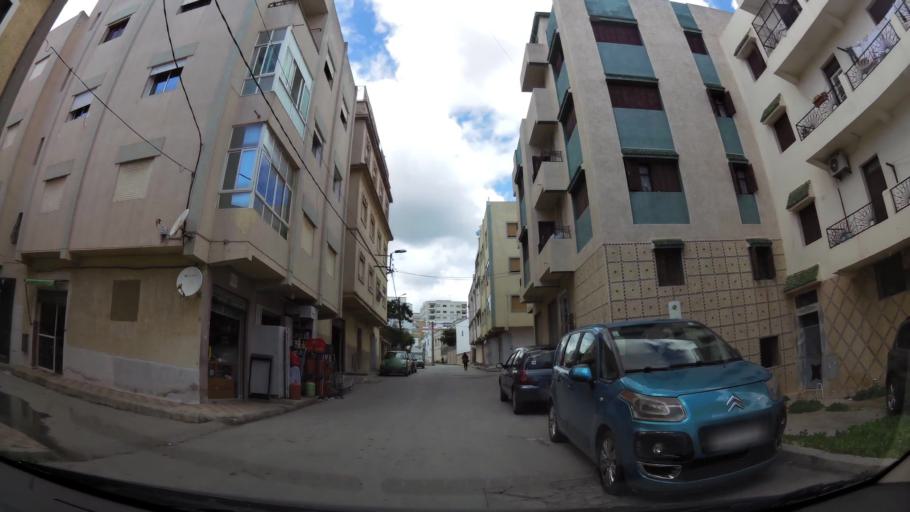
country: MA
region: Tanger-Tetouan
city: Tetouan
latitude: 35.5810
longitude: -5.3500
